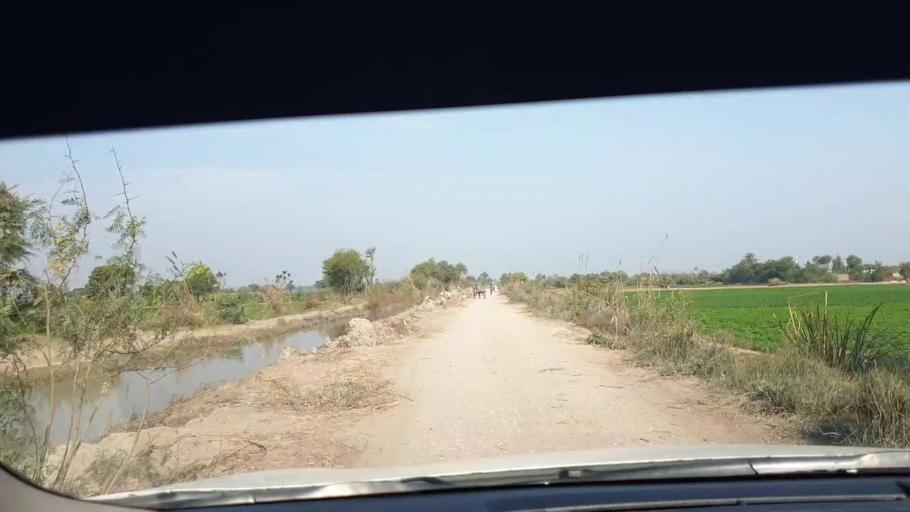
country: PK
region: Sindh
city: Tando Adam
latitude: 25.7314
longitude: 68.7026
